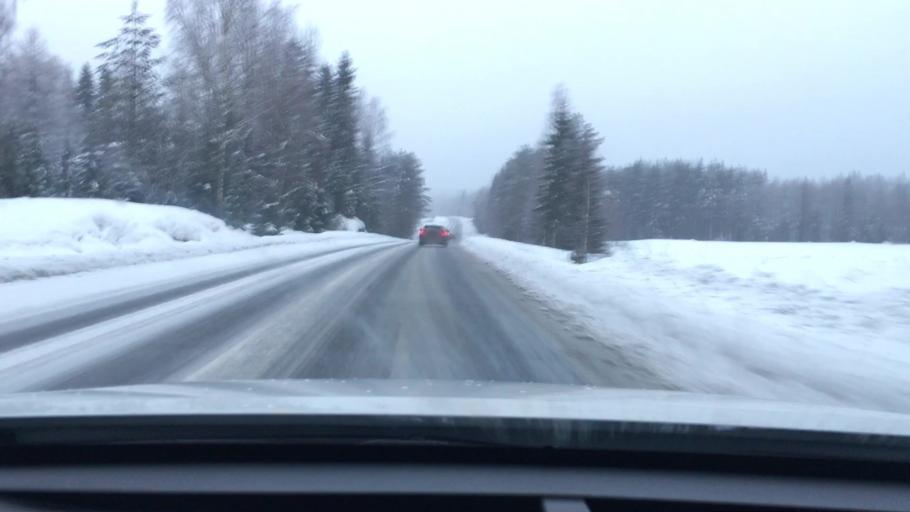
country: FI
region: Northern Savo
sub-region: Ylae-Savo
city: Sonkajaervi
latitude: 63.7623
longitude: 27.4062
